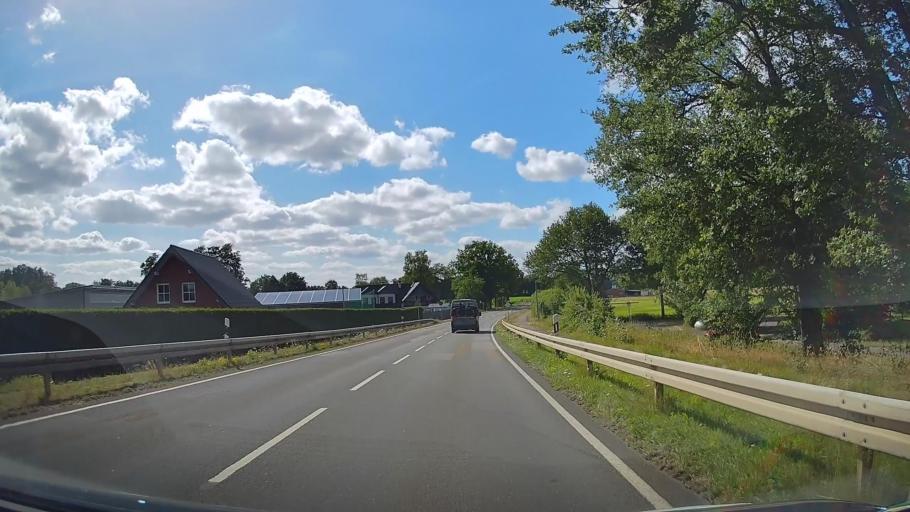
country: DE
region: Lower Saxony
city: Alfhausen
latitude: 52.4994
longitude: 7.9752
